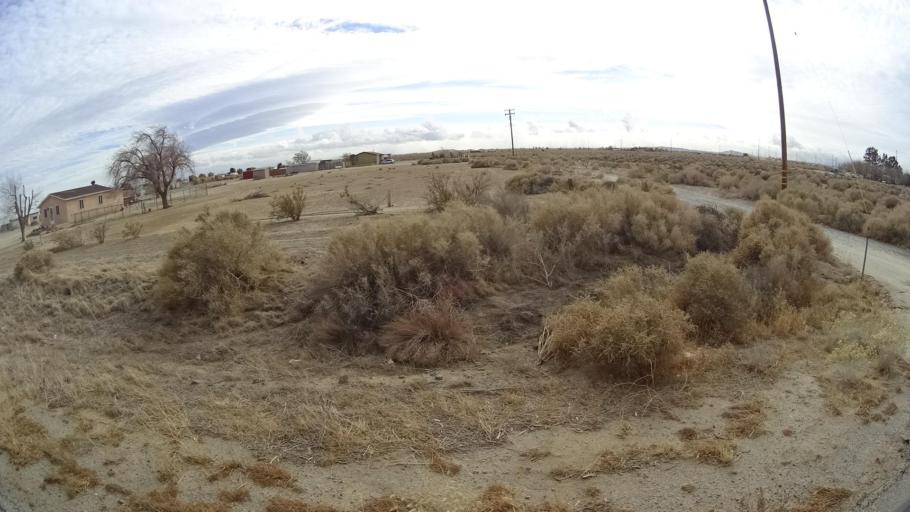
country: US
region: California
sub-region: Kern County
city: Rosamond
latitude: 34.8631
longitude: -118.3041
